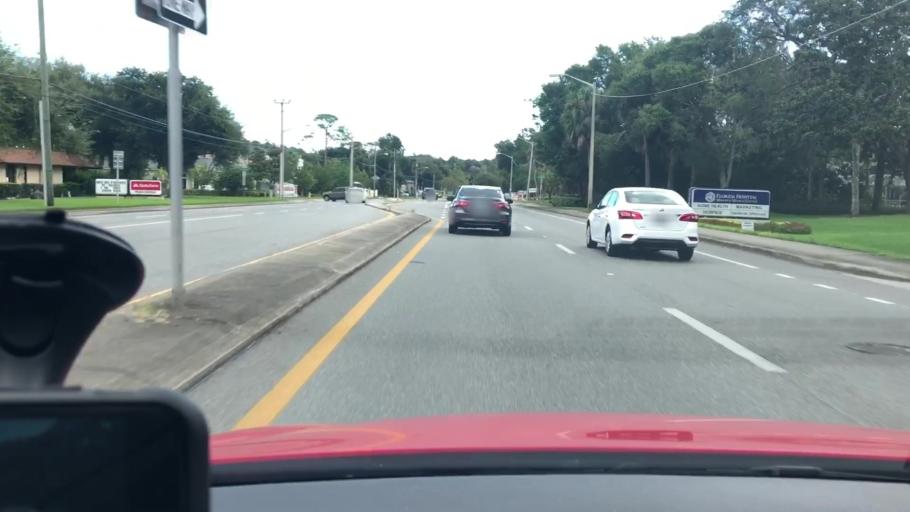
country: US
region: Florida
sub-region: Volusia County
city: Ormond Beach
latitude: 29.2788
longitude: -81.0814
